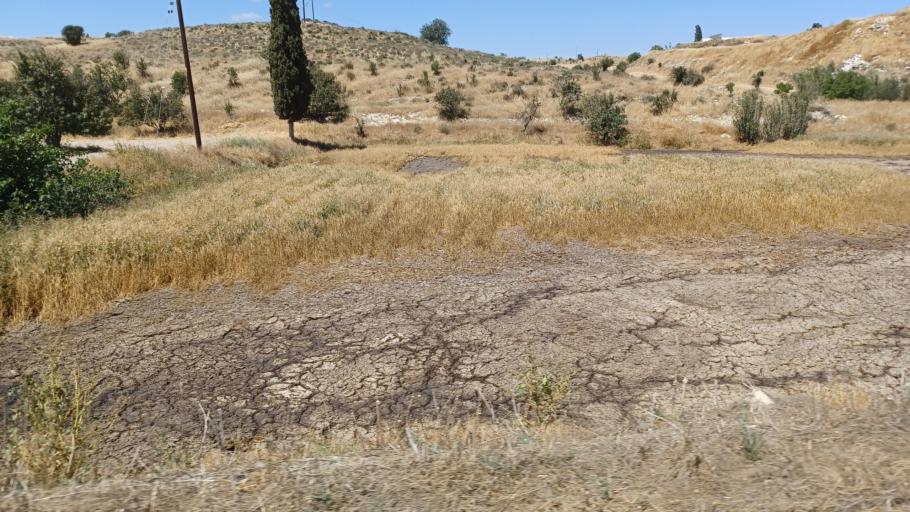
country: CY
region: Larnaka
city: Athienou
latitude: 35.0311
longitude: 33.5401
